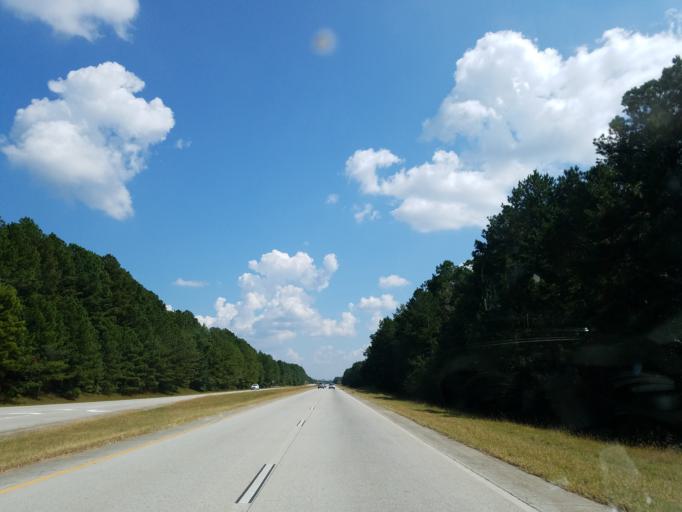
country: US
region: Georgia
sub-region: Barrow County
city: Statham
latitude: 33.9586
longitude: -83.6147
